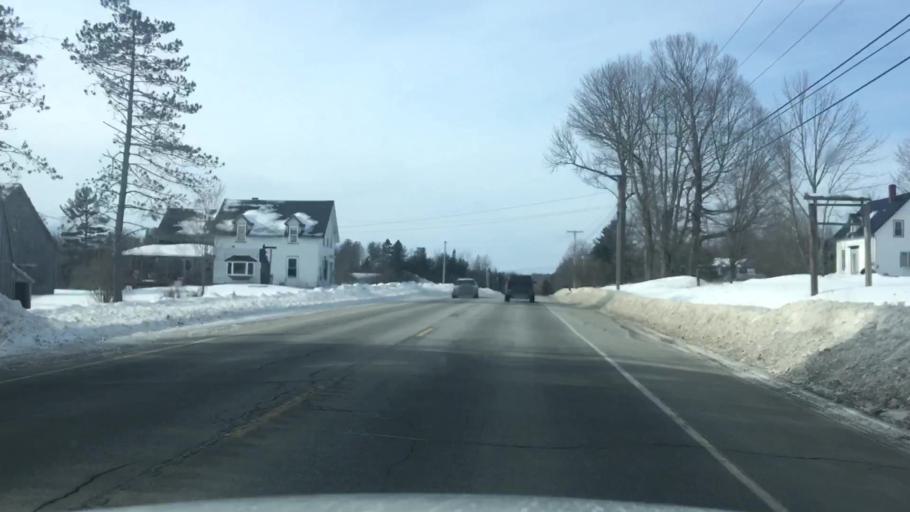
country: US
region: Maine
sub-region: Penobscot County
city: Kenduskeag
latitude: 44.9743
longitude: -68.9838
